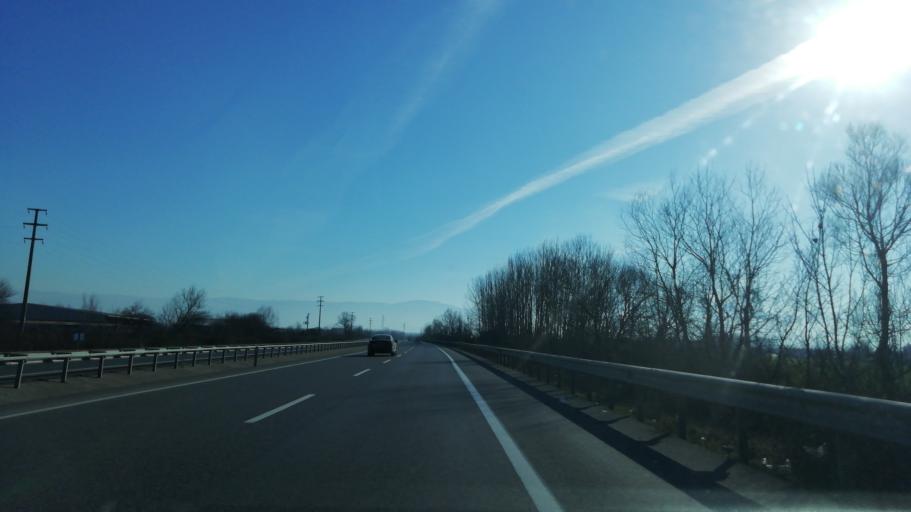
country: TR
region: Sakarya
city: Akyazi
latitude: 40.7404
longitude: 30.5643
